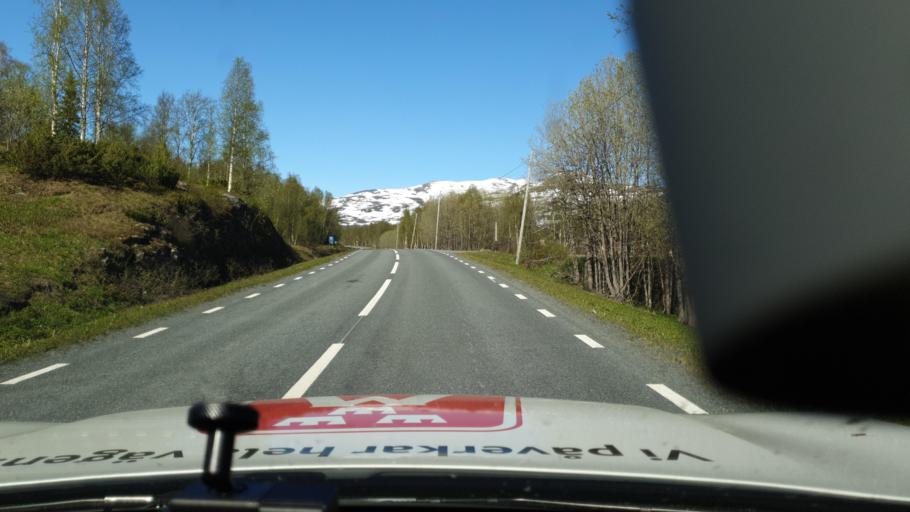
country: NO
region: Nordland
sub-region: Rana
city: Mo i Rana
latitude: 65.7542
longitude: 15.1107
